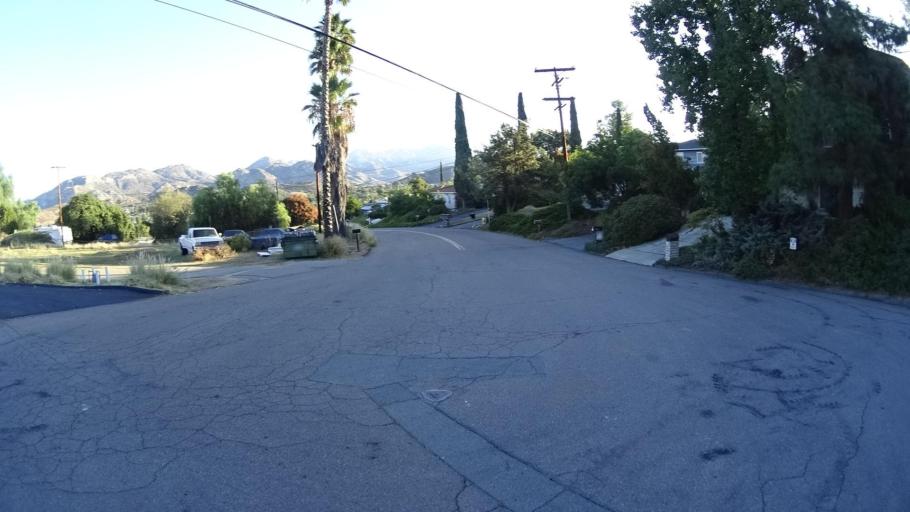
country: US
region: California
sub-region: San Diego County
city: Lakeside
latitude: 32.8508
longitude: -116.9125
